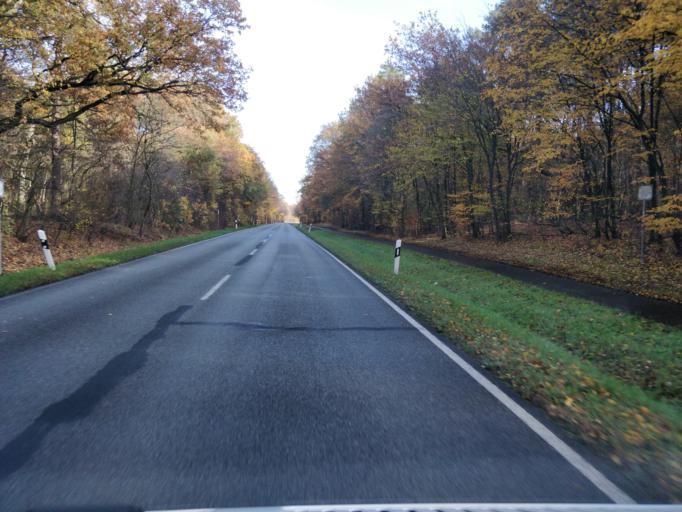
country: DE
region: North Rhine-Westphalia
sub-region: Regierungsbezirk Dusseldorf
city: Mehrhoog
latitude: 51.7192
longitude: 6.5200
